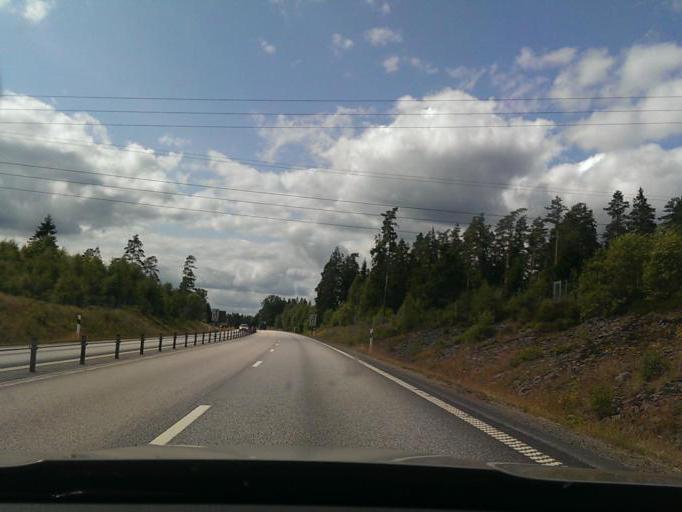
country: SE
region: Joenkoeping
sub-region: Varnamo Kommun
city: Varnamo
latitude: 57.1824
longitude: 13.9904
